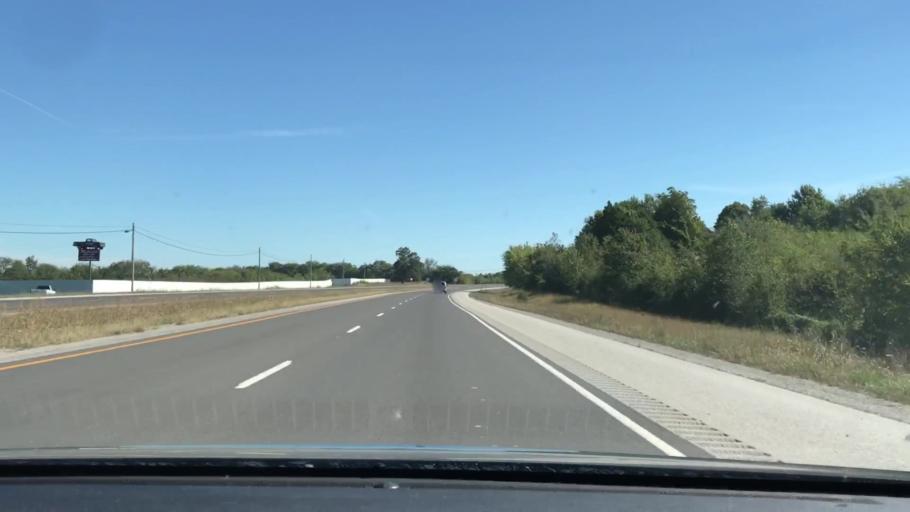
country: US
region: Kentucky
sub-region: Logan County
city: Russellville
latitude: 36.8355
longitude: -86.9630
